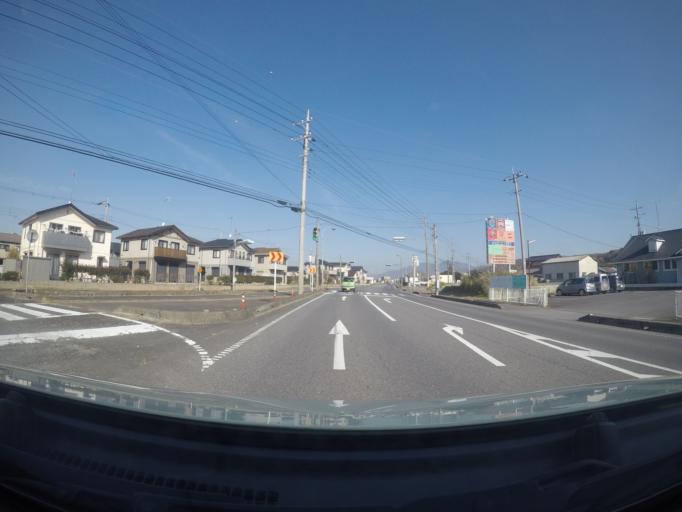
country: JP
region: Ibaraki
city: Makabe
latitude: 36.2483
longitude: 140.0697
